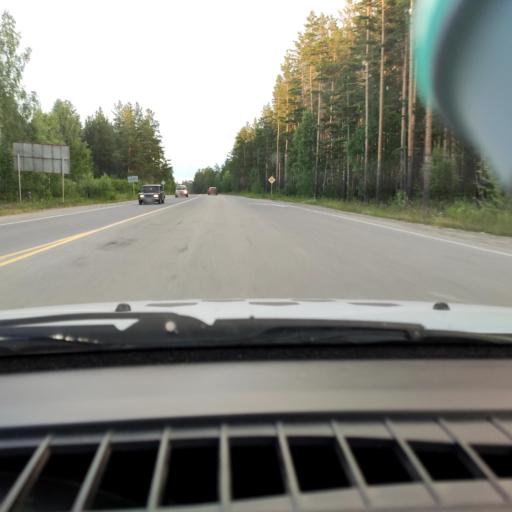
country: RU
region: Chelyabinsk
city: Kyshtym
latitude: 55.6949
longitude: 60.5017
